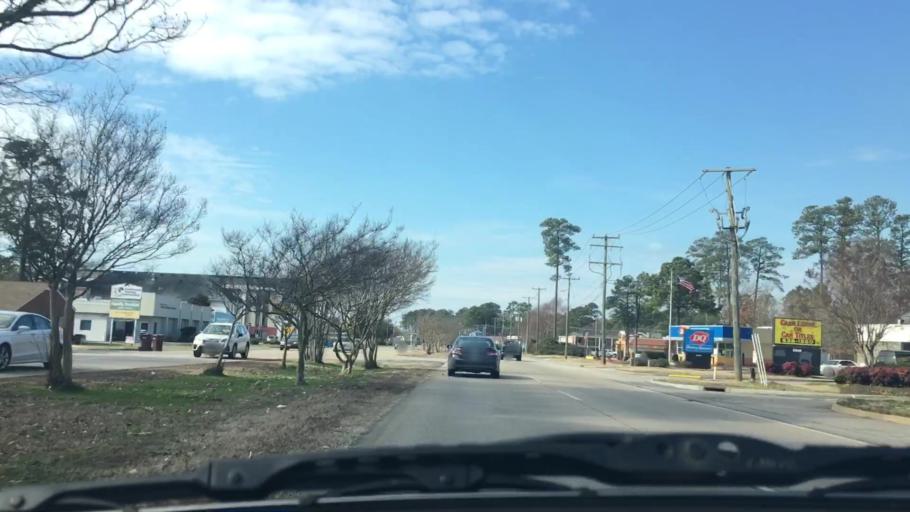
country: US
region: Virginia
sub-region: City of Portsmouth
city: Portsmouth Heights
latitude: 36.8637
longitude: -76.4052
